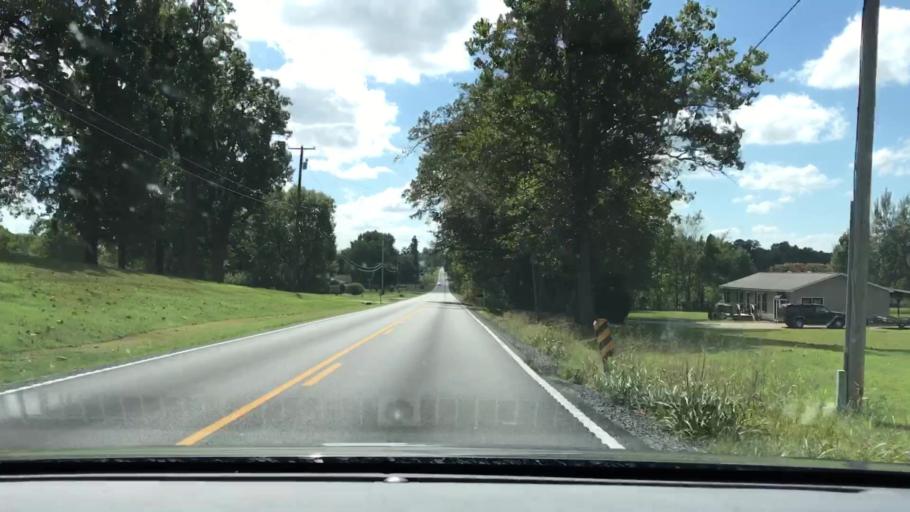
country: US
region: Kentucky
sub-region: Graves County
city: Mayfield
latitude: 36.7893
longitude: -88.5957
